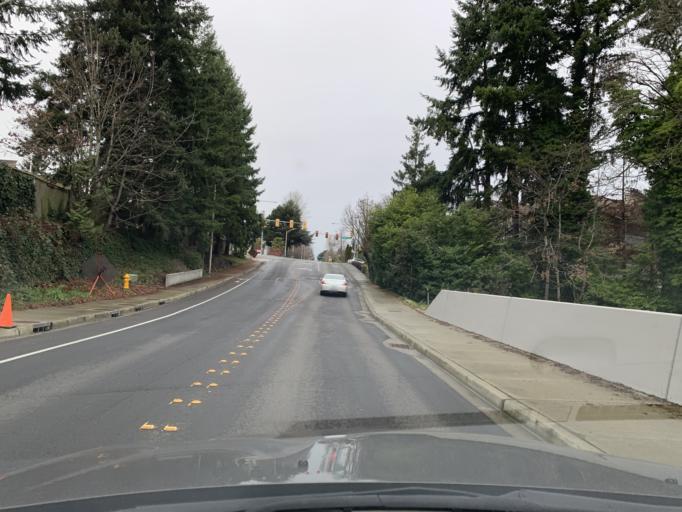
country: US
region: Washington
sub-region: King County
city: SeaTac
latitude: 47.4650
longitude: -122.2811
